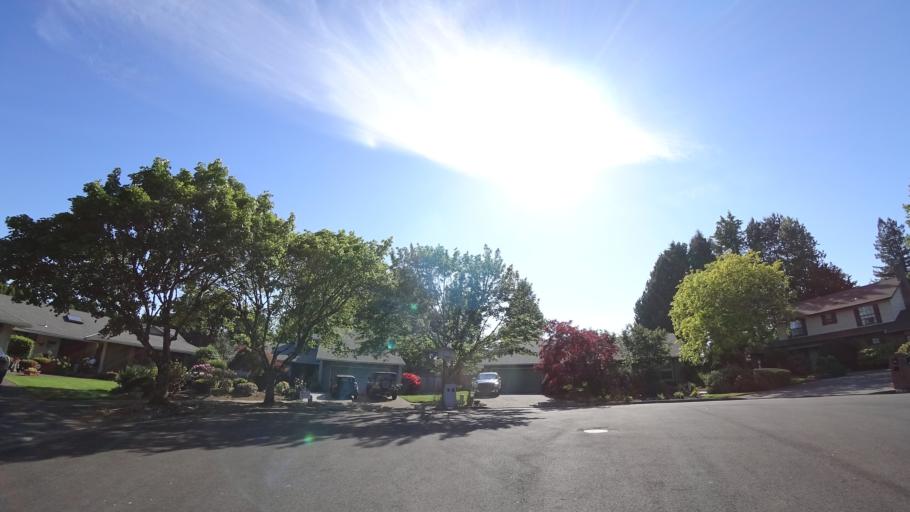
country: US
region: Oregon
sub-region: Washington County
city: Beaverton
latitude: 45.4570
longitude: -122.8068
